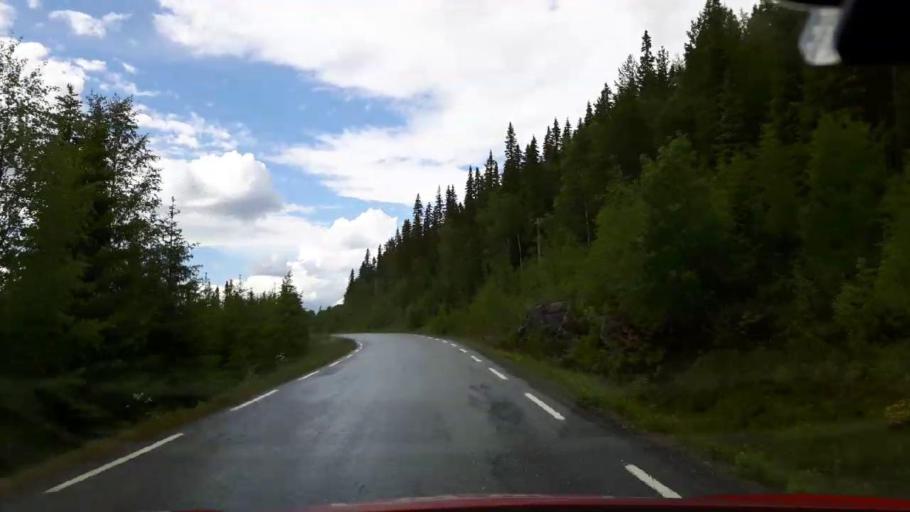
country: NO
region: Nord-Trondelag
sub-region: Lierne
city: Sandvika
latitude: 64.1031
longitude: 13.9990
